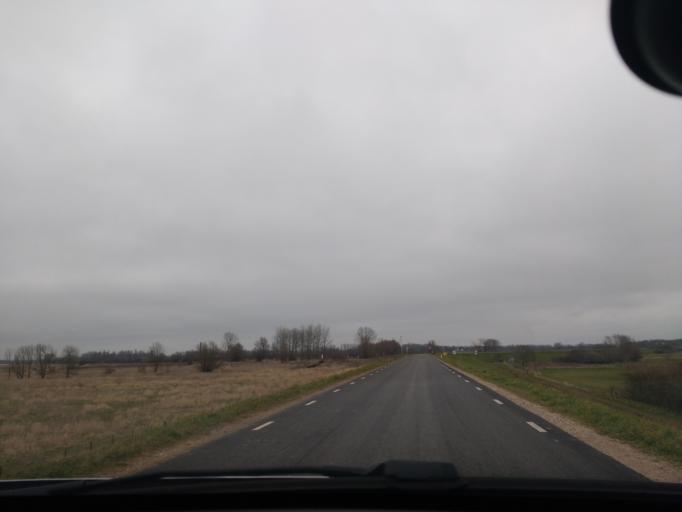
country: NL
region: Gelderland
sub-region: Gemeente Nijmegen
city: Nijmegen
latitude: 51.8494
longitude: 5.8832
